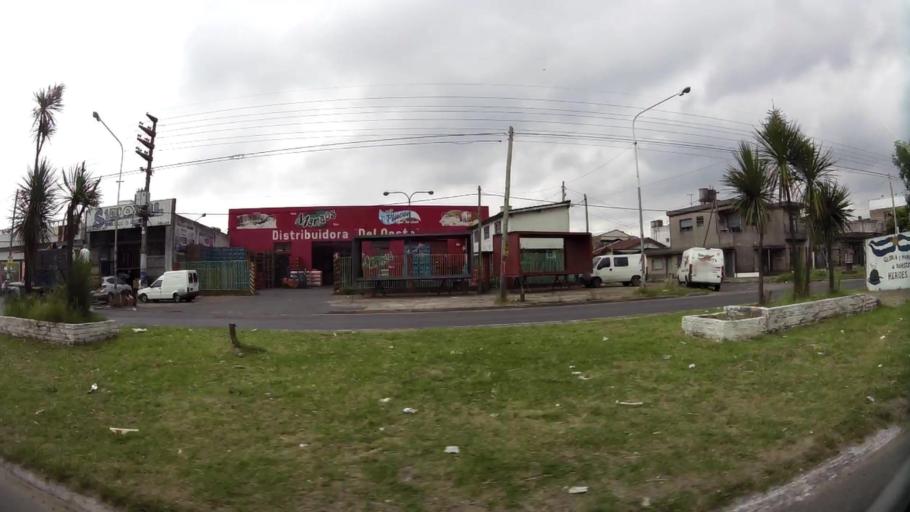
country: AR
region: Buenos Aires
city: San Justo
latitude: -34.6965
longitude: -58.5356
